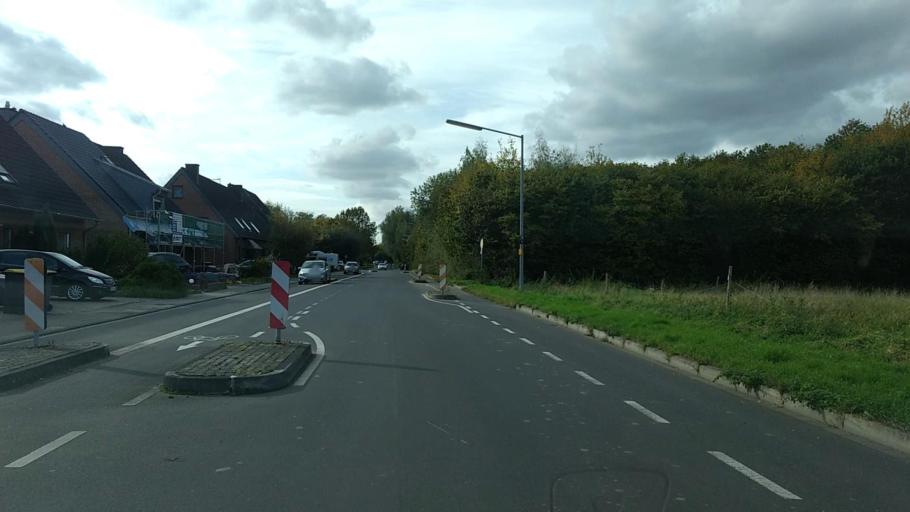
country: DE
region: North Rhine-Westphalia
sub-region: Regierungsbezirk Koln
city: Bergheim
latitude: 50.9395
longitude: 6.6708
